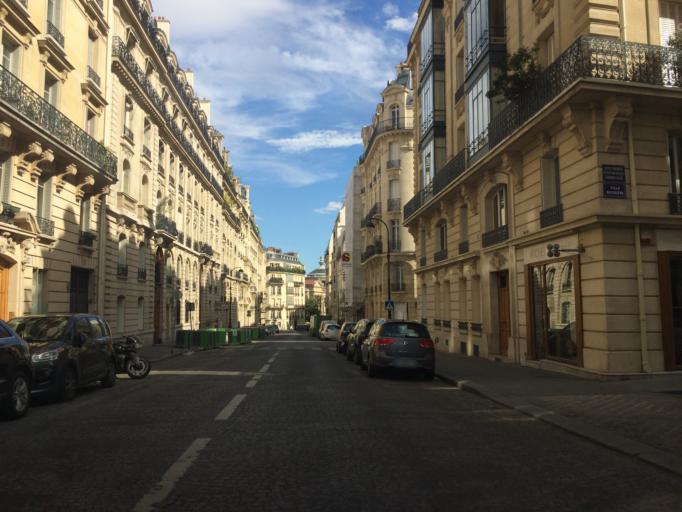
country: FR
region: Ile-de-France
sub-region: Departement des Hauts-de-Seine
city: Levallois-Perret
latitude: 48.8665
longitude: 2.2906
